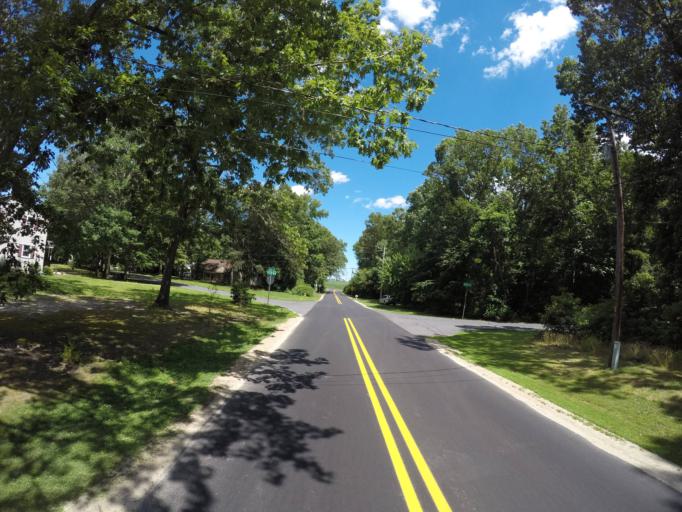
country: US
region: Delaware
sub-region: Sussex County
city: Milford
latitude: 38.9308
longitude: -75.4106
